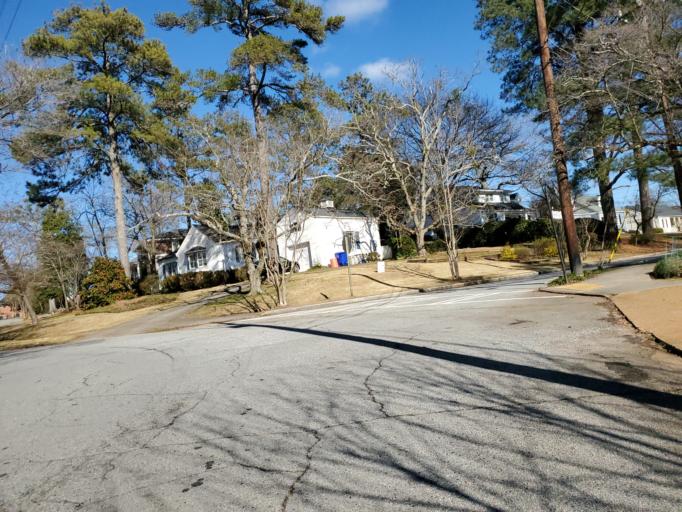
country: US
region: Georgia
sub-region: DeKalb County
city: Avondale Estates
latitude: 33.7723
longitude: -84.2635
